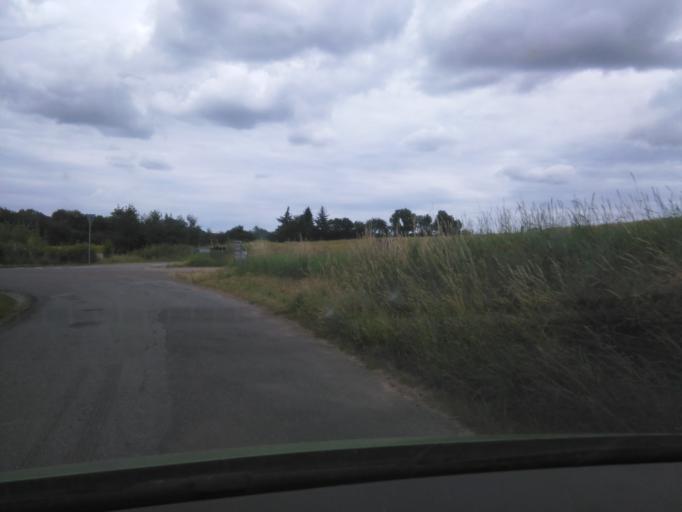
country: DK
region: Central Jutland
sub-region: Arhus Kommune
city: Marslet
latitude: 56.0263
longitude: 10.1460
